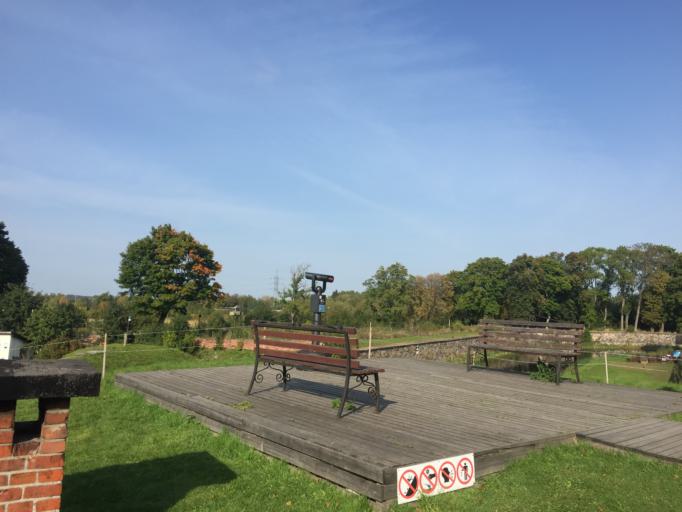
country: RU
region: Kaliningrad
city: Bol'shoe Isakovo
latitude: 54.6569
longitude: 20.5674
